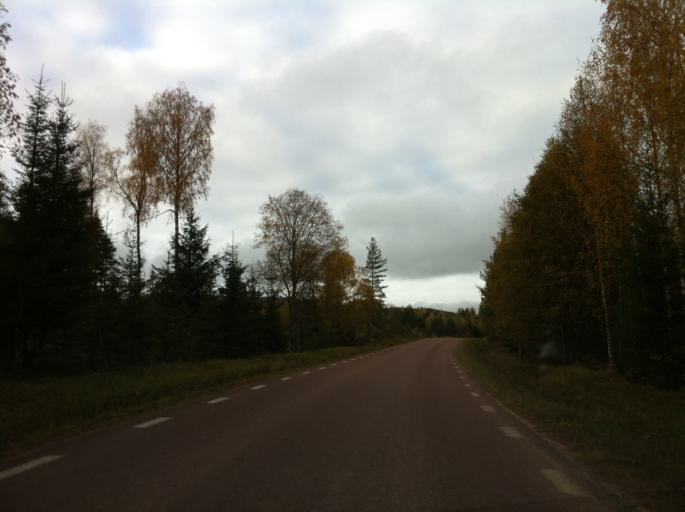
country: SE
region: Dalarna
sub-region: Mora Kommun
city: Mora
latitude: 61.0851
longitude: 14.3805
